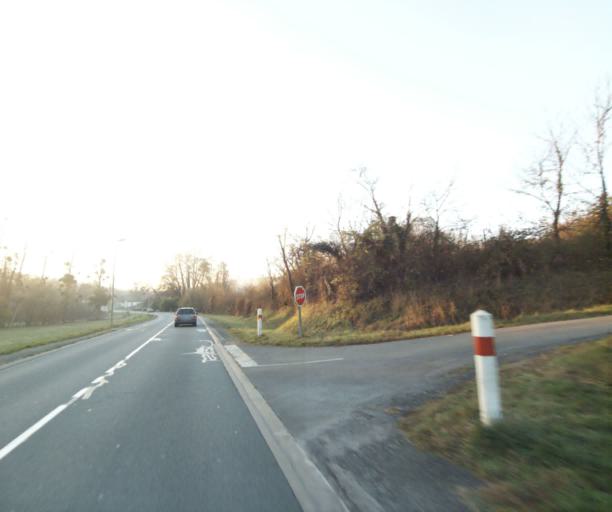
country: FR
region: Poitou-Charentes
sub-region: Departement de la Charente-Maritime
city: Chaniers
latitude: 45.7343
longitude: -0.5379
